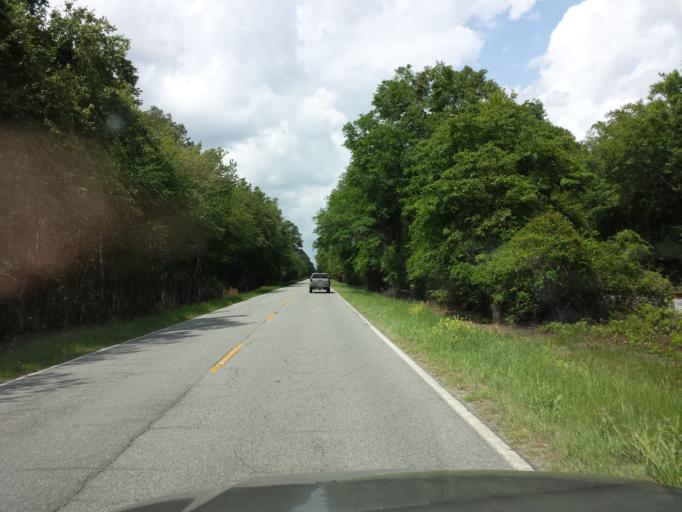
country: US
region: Georgia
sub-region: Echols County
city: Statenville
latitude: 30.6661
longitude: -83.1609
